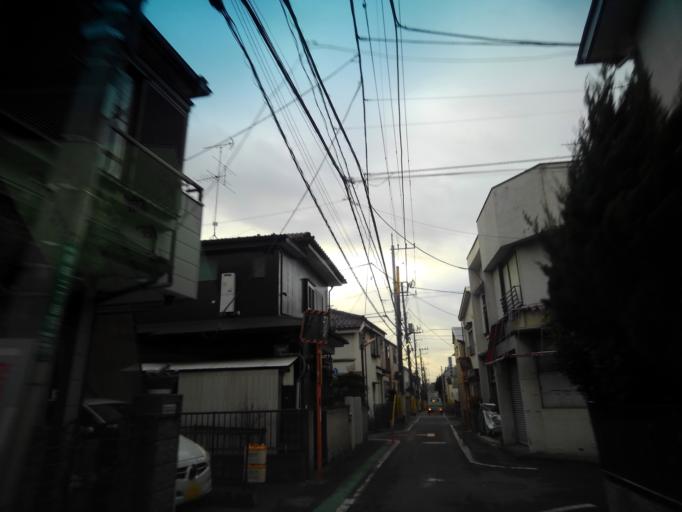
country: JP
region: Tokyo
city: Kokubunji
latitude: 35.7137
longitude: 139.4492
